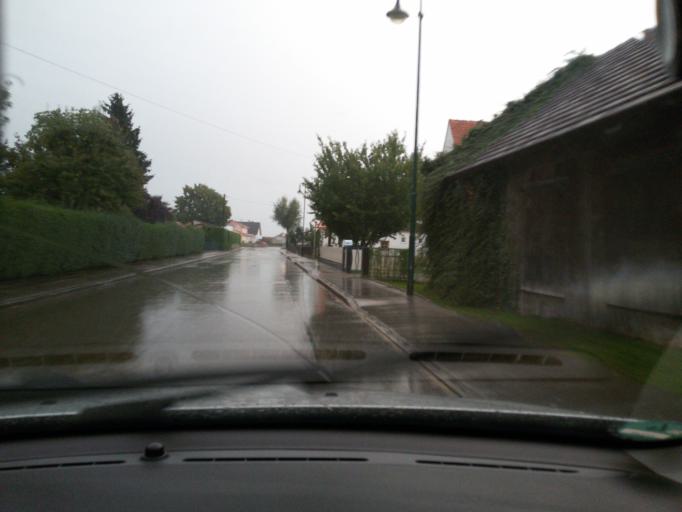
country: DE
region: Bavaria
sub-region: Swabia
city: Hiltenfingen
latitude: 48.1614
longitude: 10.7225
